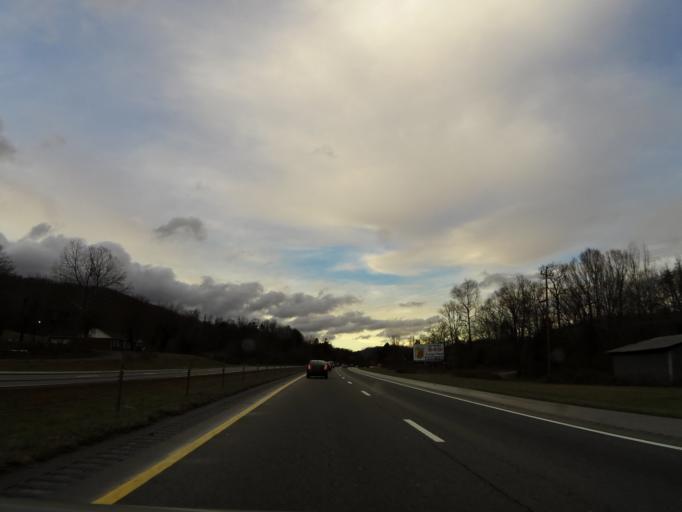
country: US
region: Tennessee
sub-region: Anderson County
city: Rocky Top
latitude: 36.2499
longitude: -84.1817
